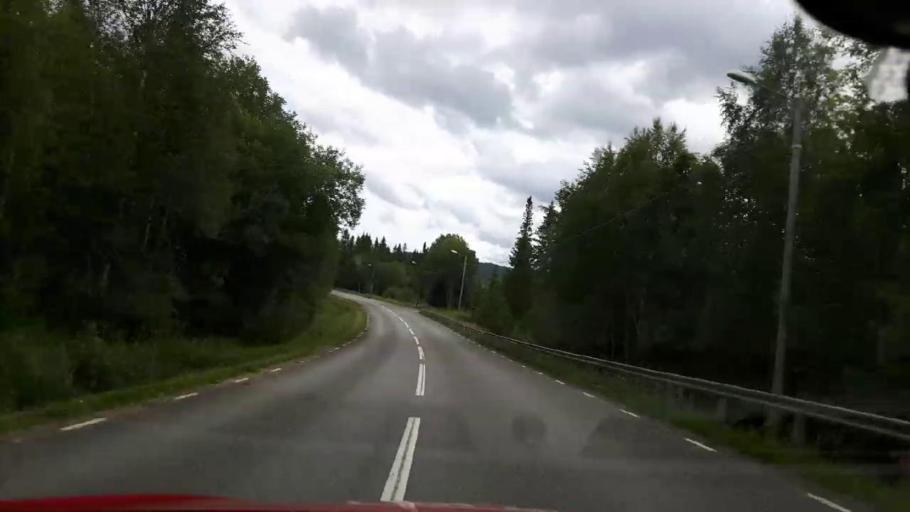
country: NO
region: Nord-Trondelag
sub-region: Lierne
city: Sandvika
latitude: 64.3912
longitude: 14.3734
